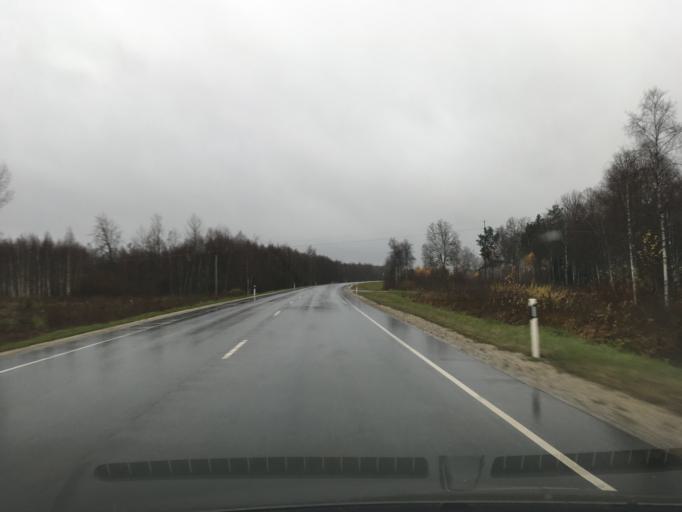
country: EE
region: Harju
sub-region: Nissi vald
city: Turba
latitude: 58.8524
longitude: 24.0693
